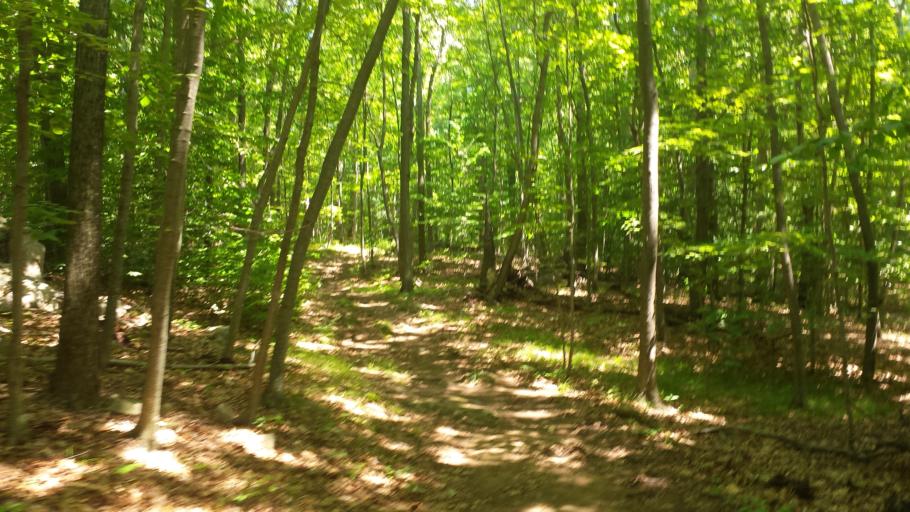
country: US
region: New York
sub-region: Westchester County
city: Pound Ridge
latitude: 41.2662
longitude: -73.5868
